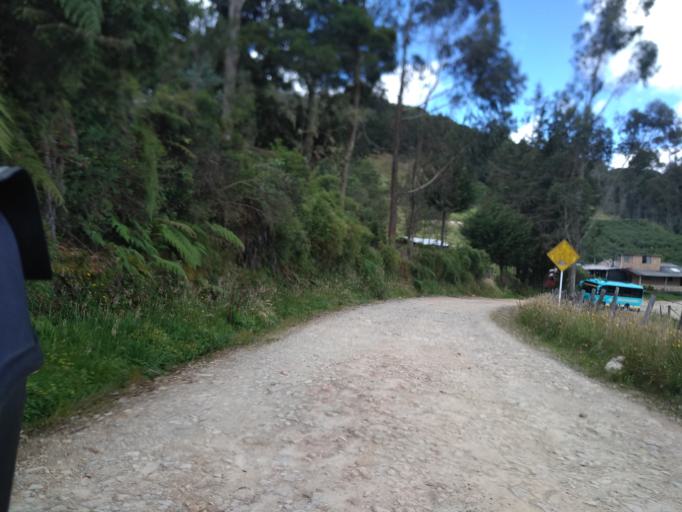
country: CO
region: Boyaca
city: Duitama
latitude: 5.9400
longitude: -73.1202
